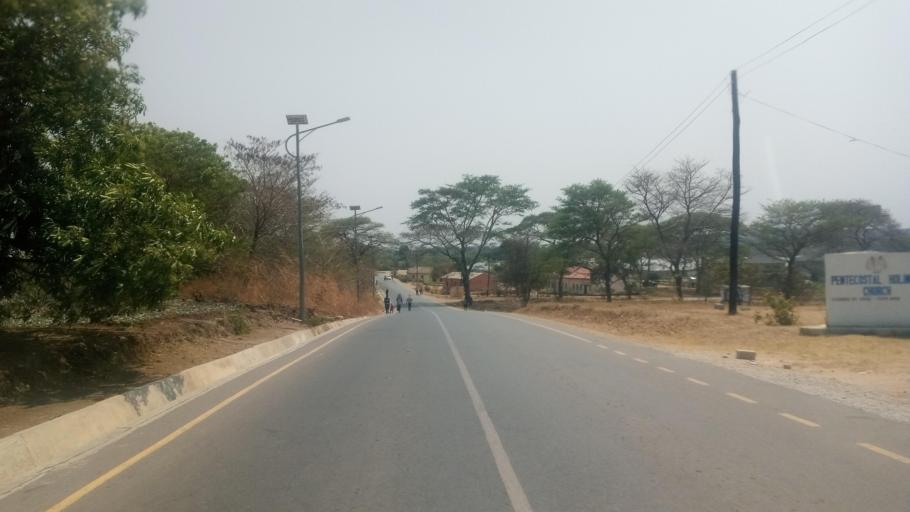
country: ZM
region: Lusaka
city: Lusaka
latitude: -15.4517
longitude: 28.4412
